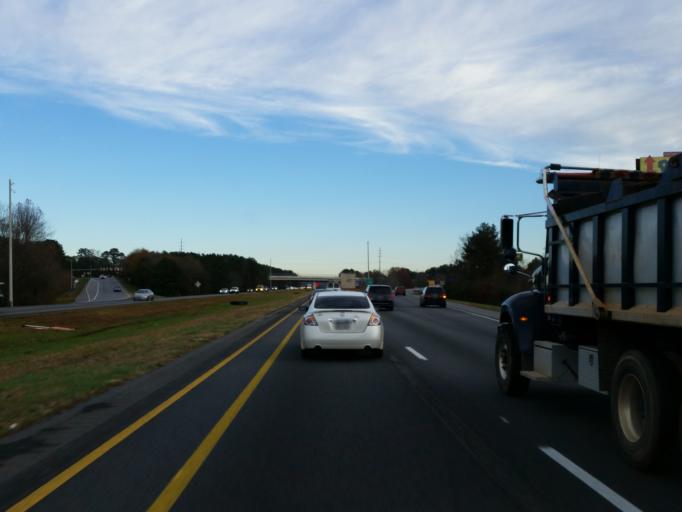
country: US
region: Georgia
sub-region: Cherokee County
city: Woodstock
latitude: 34.0807
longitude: -84.5373
